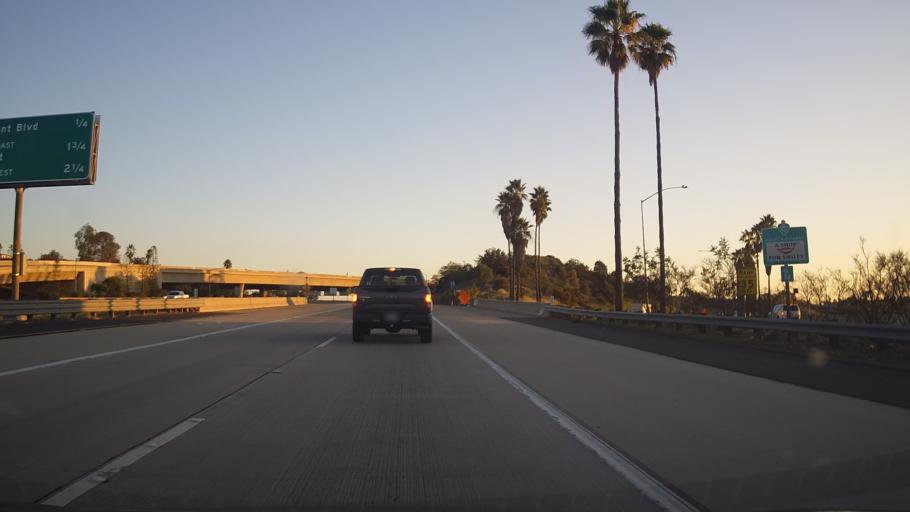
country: US
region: California
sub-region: San Diego County
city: La Mesa
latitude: 32.7806
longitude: -117.0048
